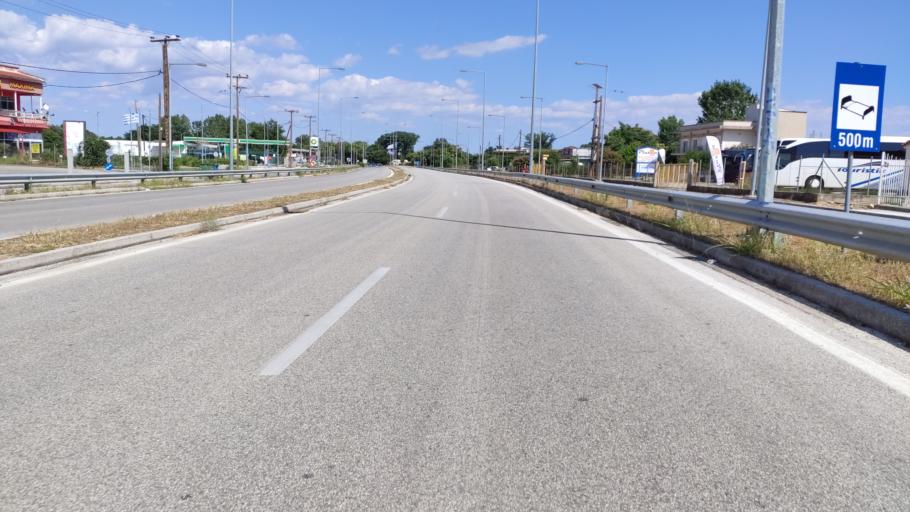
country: GR
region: East Macedonia and Thrace
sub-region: Nomos Rodopis
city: Komotini
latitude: 41.1138
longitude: 25.3824
